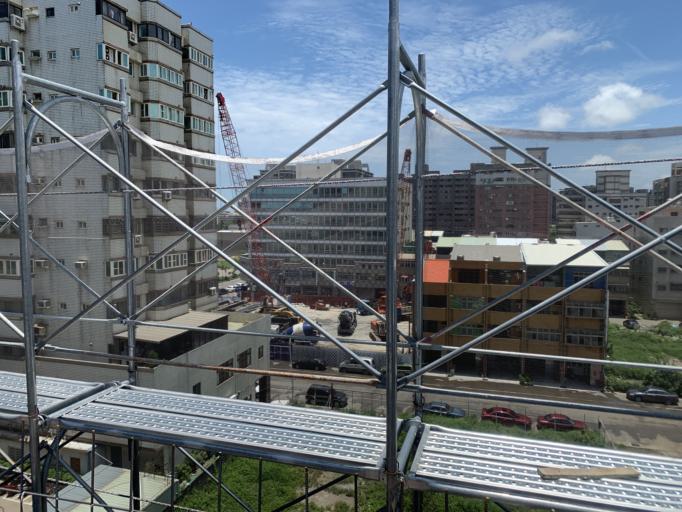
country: TW
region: Taiwan
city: Fengyuan
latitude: 24.2614
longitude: 120.5327
